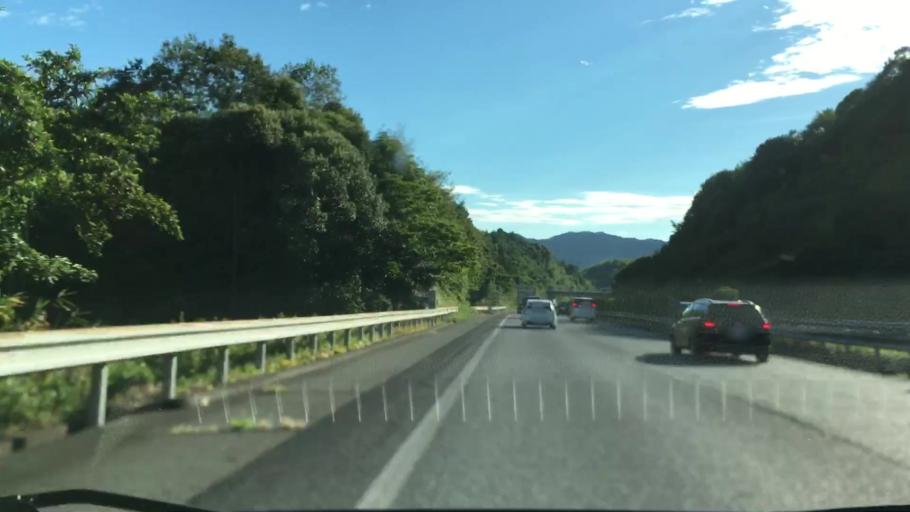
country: JP
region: Yamaguchi
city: Hikari
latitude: 34.0427
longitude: 131.9907
